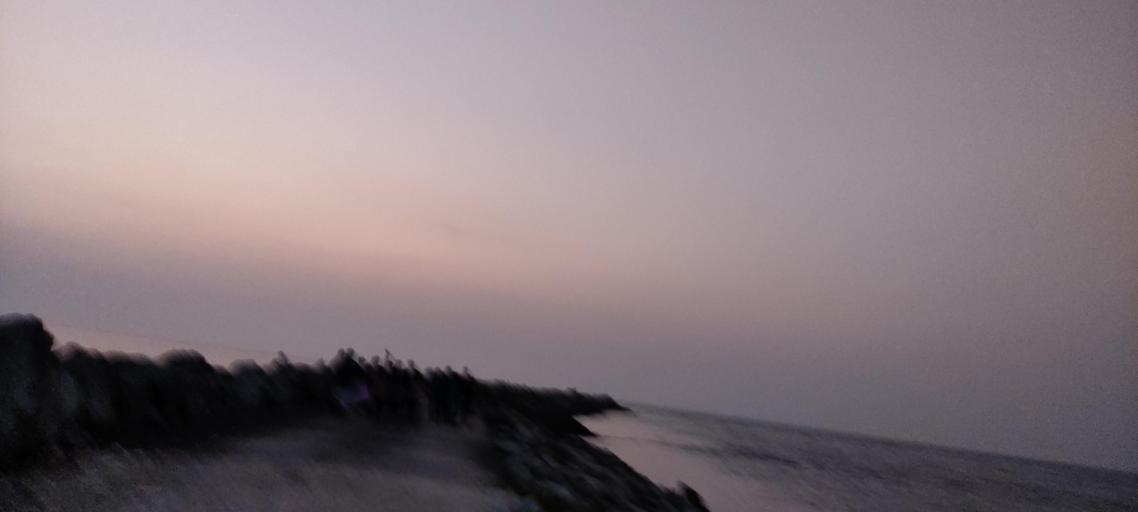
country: IN
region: Kerala
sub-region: Alappuzha
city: Kayankulam
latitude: 9.1349
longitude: 76.4611
